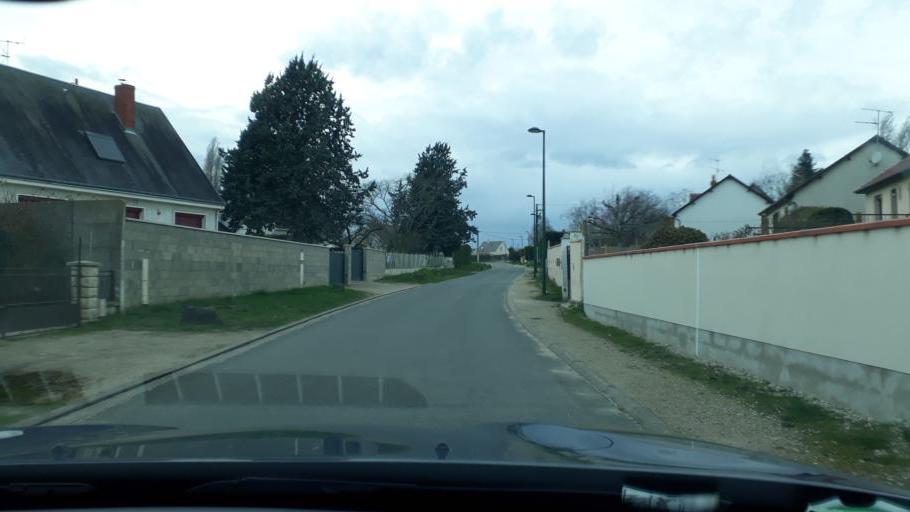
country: FR
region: Centre
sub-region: Departement du Loiret
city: Loury
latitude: 48.0046
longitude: 2.0949
